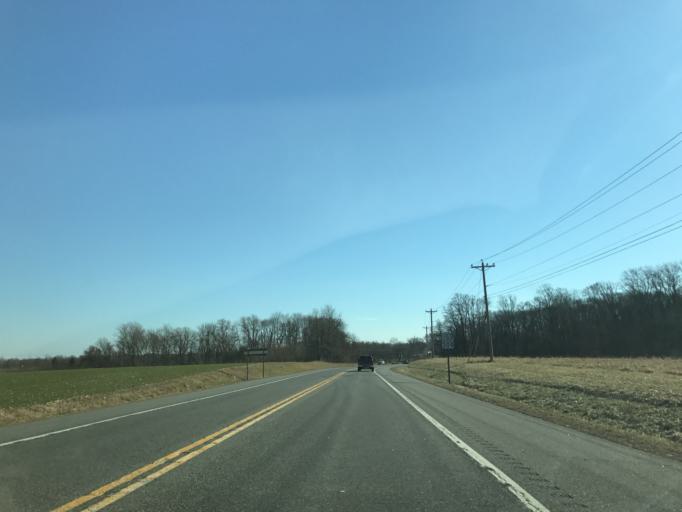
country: US
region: Maryland
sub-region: Queen Anne's County
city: Centreville
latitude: 39.0036
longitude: -76.0740
